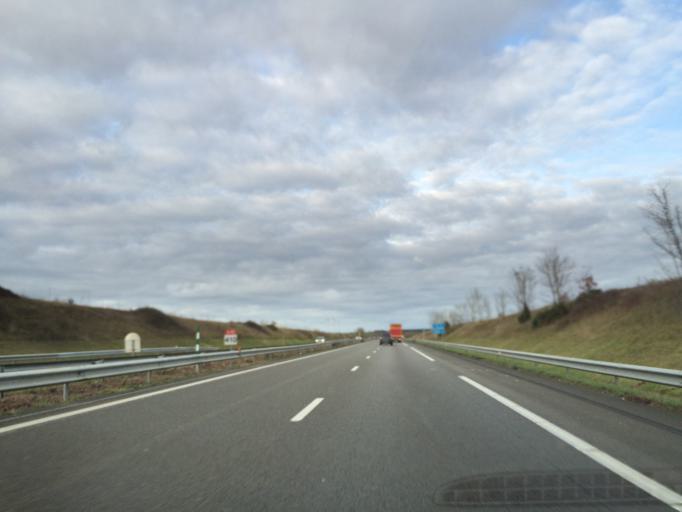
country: FR
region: Poitou-Charentes
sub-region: Departement de la Charente-Maritime
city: Saint-Jean-d'Angely
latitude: 45.9881
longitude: -0.5447
